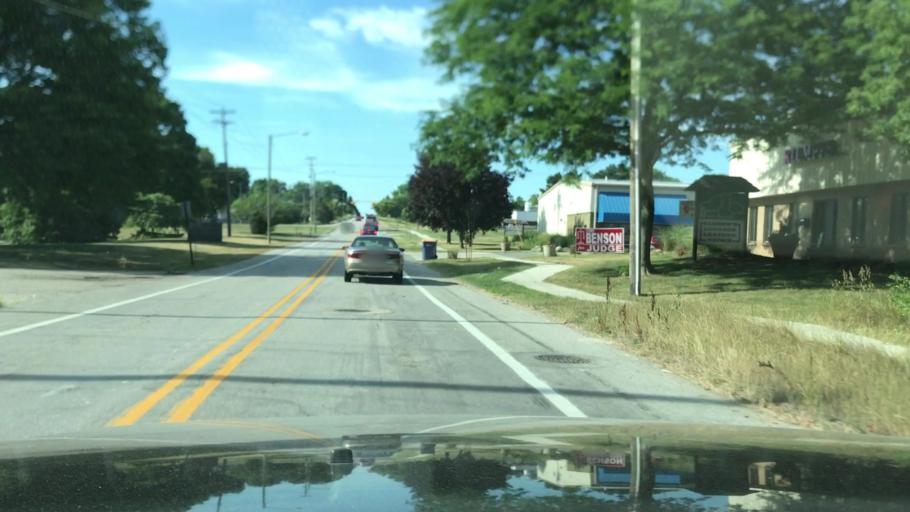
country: US
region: Michigan
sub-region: Kent County
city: East Grand Rapids
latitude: 42.9731
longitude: -85.6104
